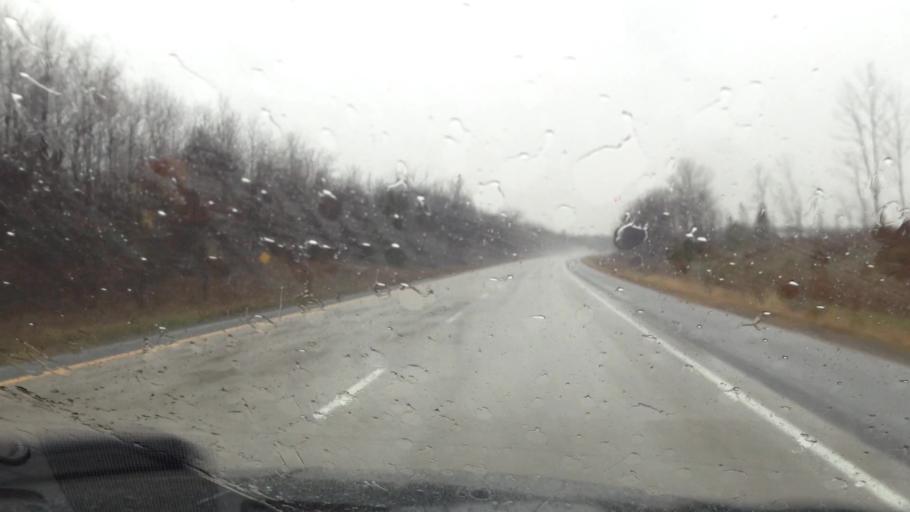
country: CA
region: Ontario
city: Hawkesbury
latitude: 45.5016
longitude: -74.5961
